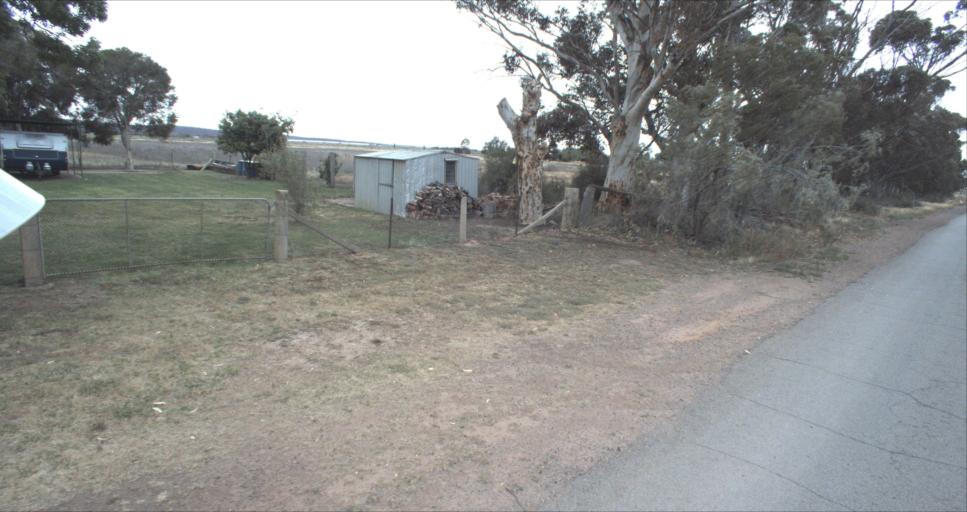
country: AU
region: New South Wales
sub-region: Leeton
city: Leeton
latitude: -34.4043
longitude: 146.3415
